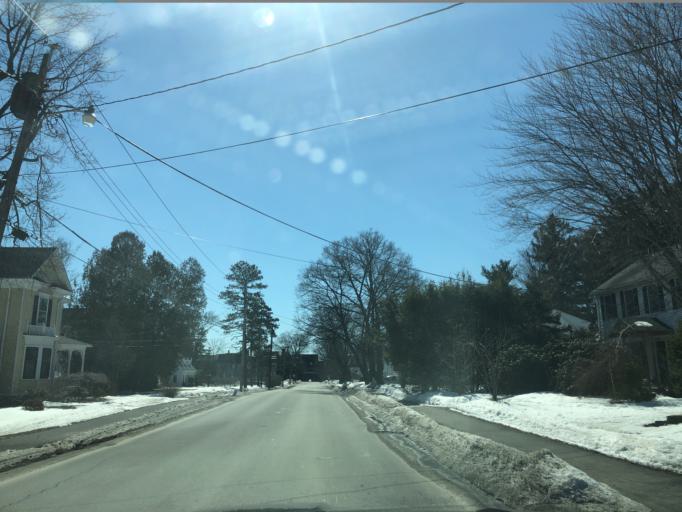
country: US
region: Maine
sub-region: Penobscot County
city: Brewer
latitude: 44.8126
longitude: -68.7528
